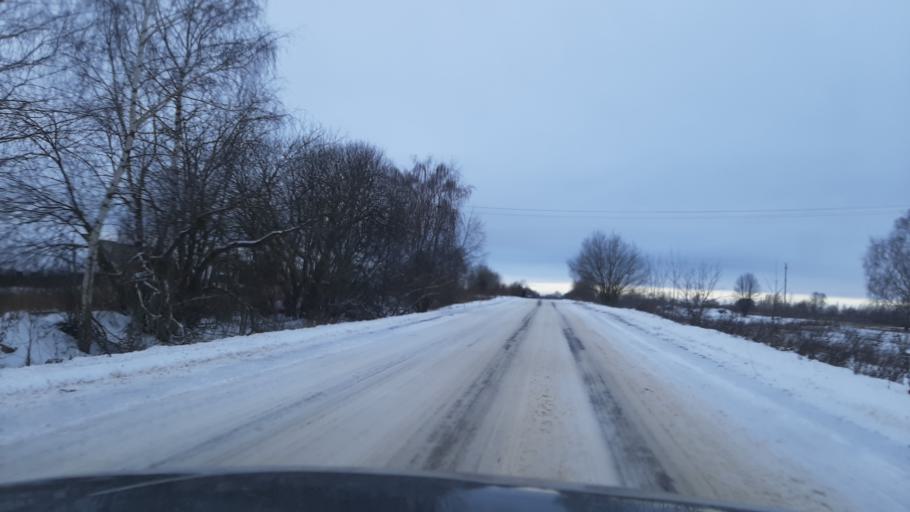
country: RU
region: Kostroma
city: Volgorechensk
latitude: 57.4350
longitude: 41.0644
